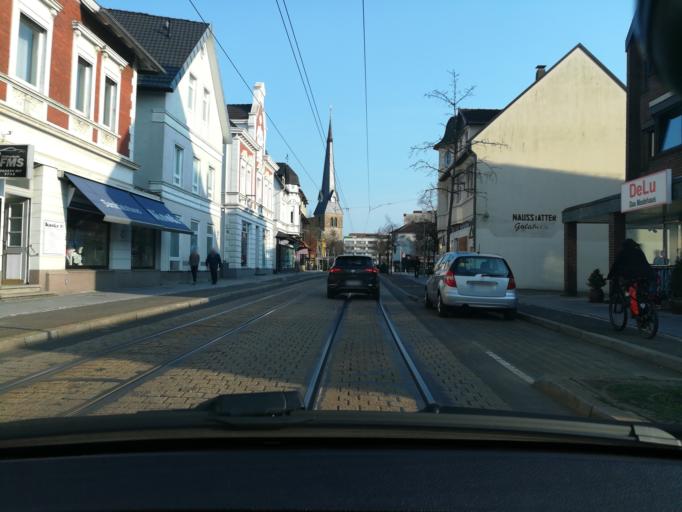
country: DE
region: North Rhine-Westphalia
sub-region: Regierungsbezirk Detmold
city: Bielefeld
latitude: 51.9898
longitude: 8.5120
